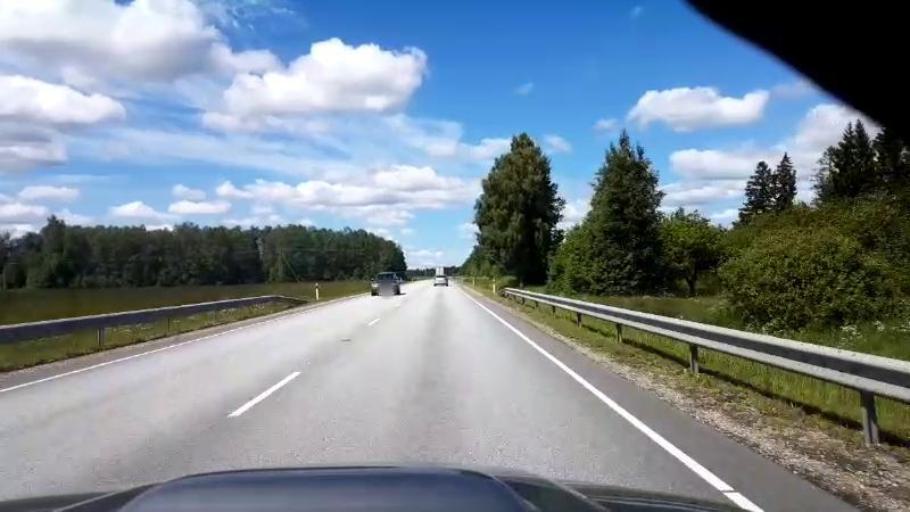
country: EE
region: Paernumaa
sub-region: Halinga vald
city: Parnu-Jaagupi
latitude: 58.5622
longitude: 24.5186
